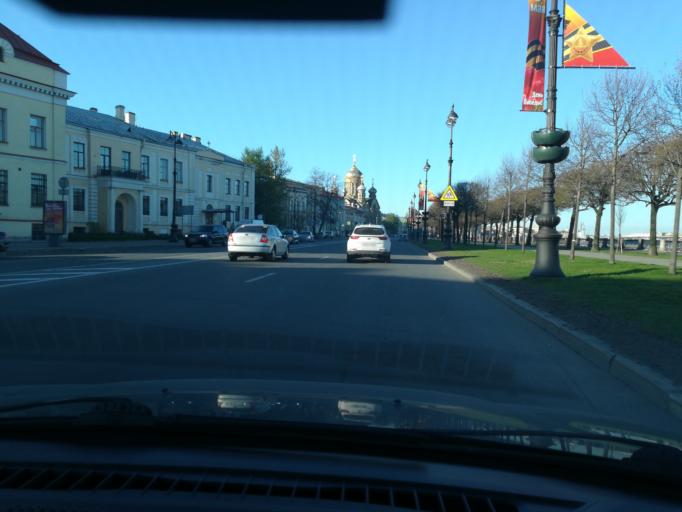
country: RU
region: St.-Petersburg
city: Vasyl'evsky Ostrov
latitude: 59.9311
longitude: 30.2723
